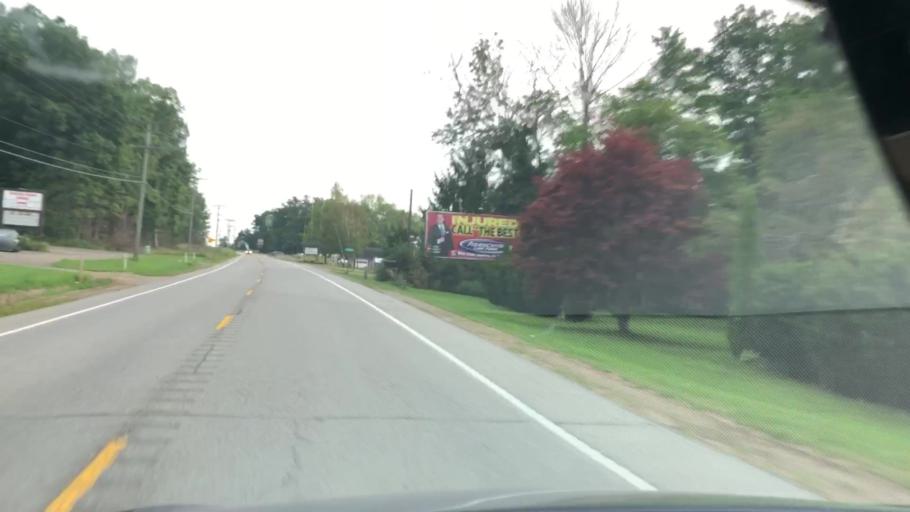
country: US
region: Pennsylvania
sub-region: Crawford County
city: Titusville
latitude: 41.5920
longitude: -79.6835
